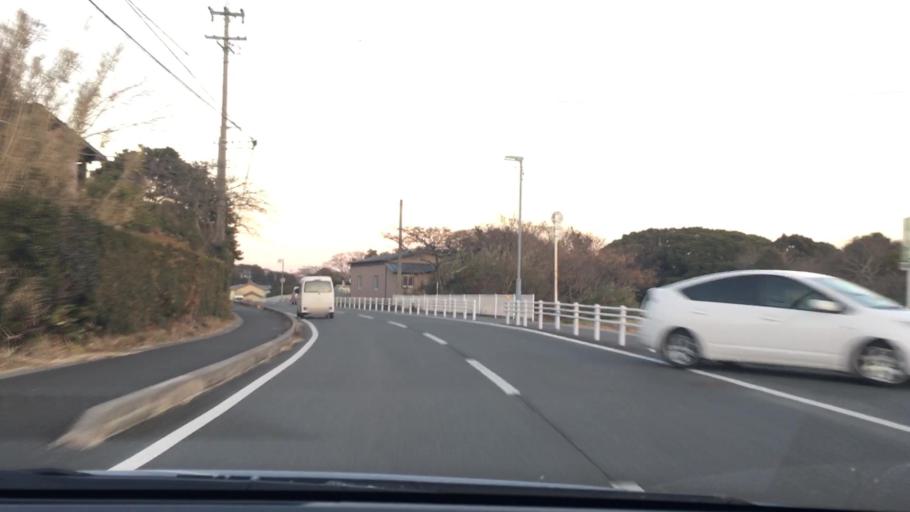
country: JP
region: Aichi
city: Tahara
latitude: 34.6702
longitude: 137.2565
